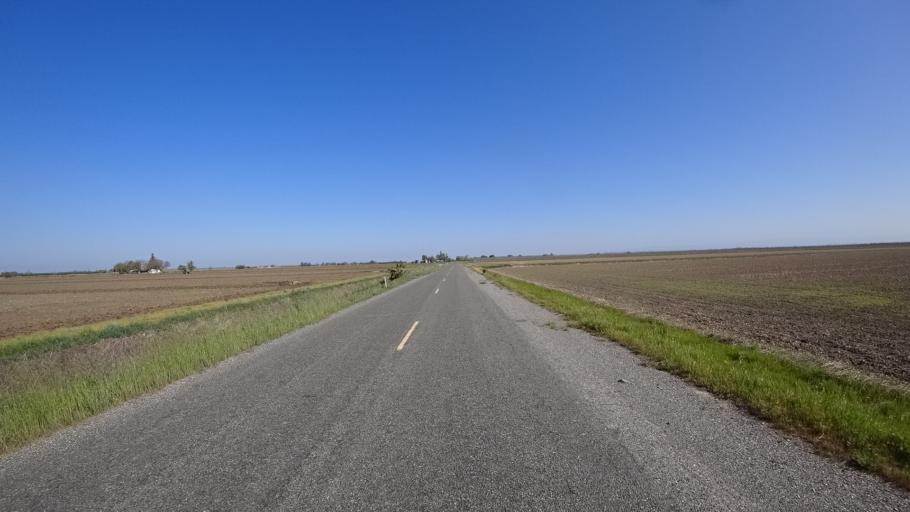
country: US
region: California
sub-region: Glenn County
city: Hamilton City
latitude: 39.6066
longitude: -122.0276
